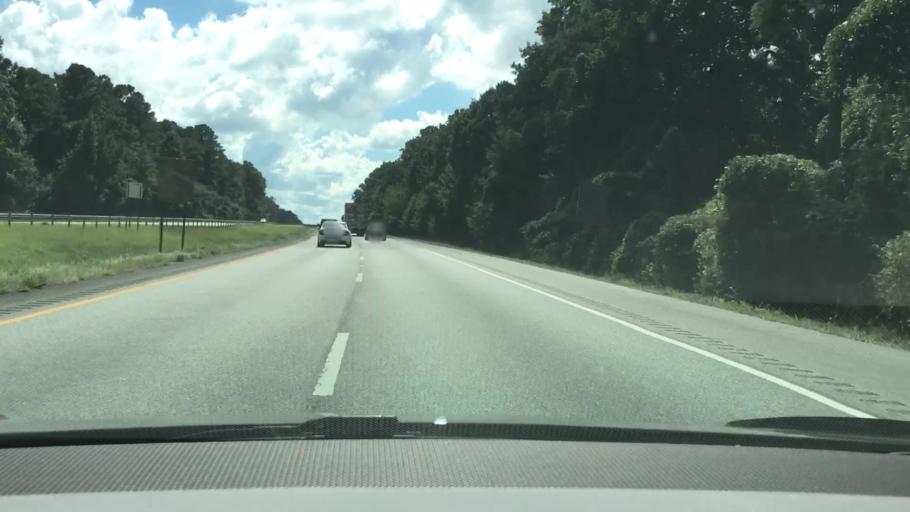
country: US
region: Alabama
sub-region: Lee County
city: Auburn
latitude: 32.5942
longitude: -85.4523
